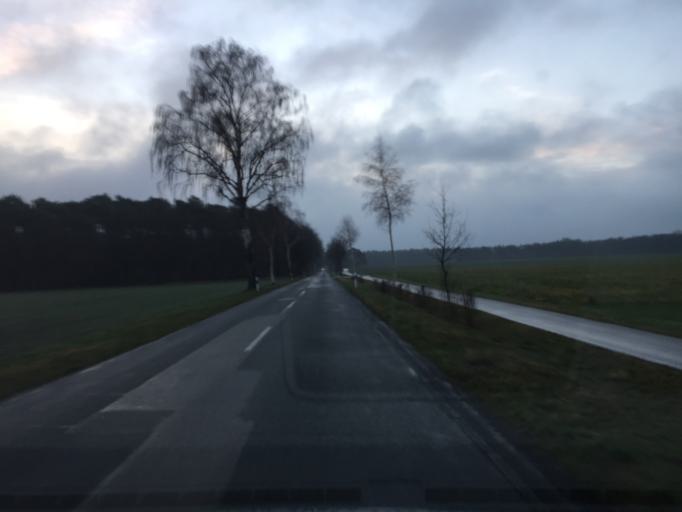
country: DE
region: Lower Saxony
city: Pennigsehl
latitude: 52.6214
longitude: 9.0602
